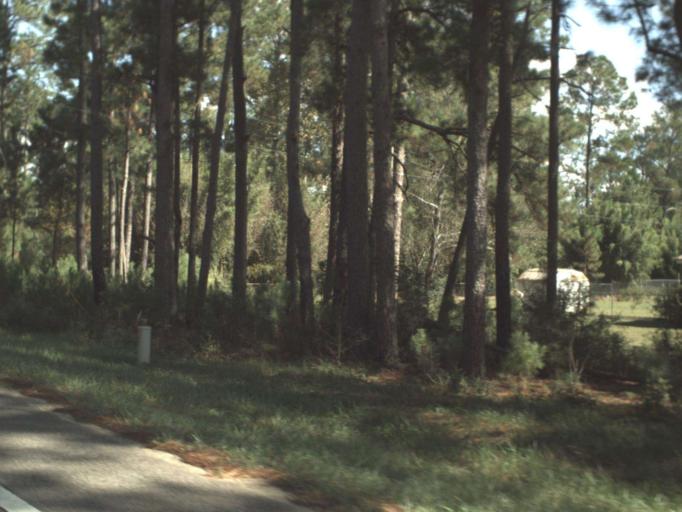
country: US
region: Florida
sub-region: Walton County
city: DeFuniak Springs
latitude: 30.8548
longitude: -86.1156
